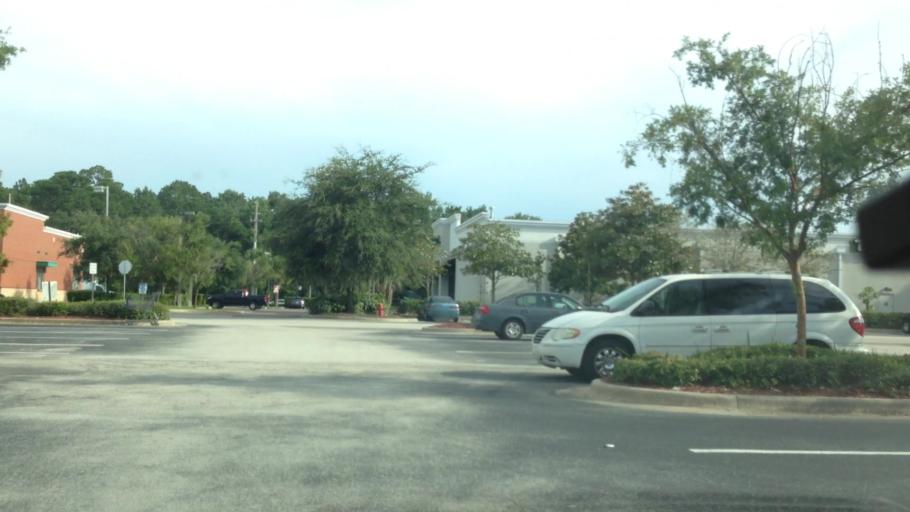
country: US
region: Florida
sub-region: Duval County
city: Atlantic Beach
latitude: 30.3210
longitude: -81.4675
